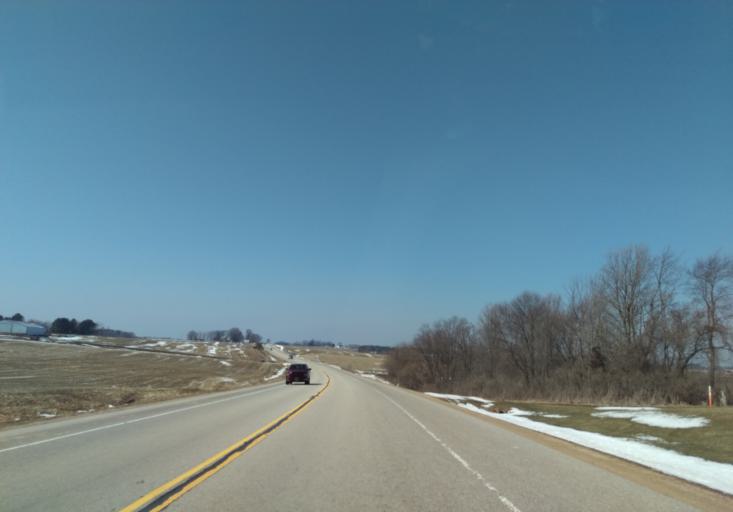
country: US
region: Wisconsin
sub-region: Vernon County
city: Viroqua
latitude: 43.4248
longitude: -90.6608
